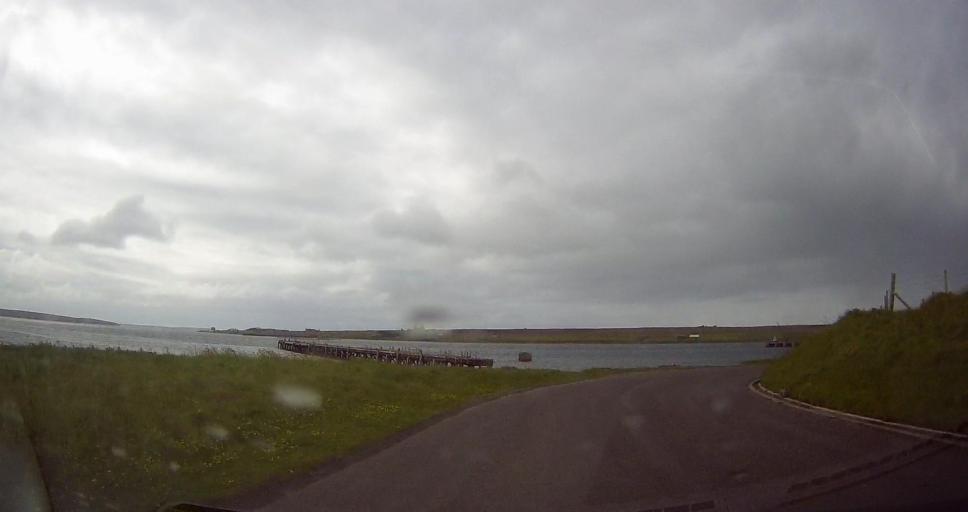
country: GB
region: Scotland
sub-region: Orkney Islands
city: Stromness
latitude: 58.8333
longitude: -3.1951
